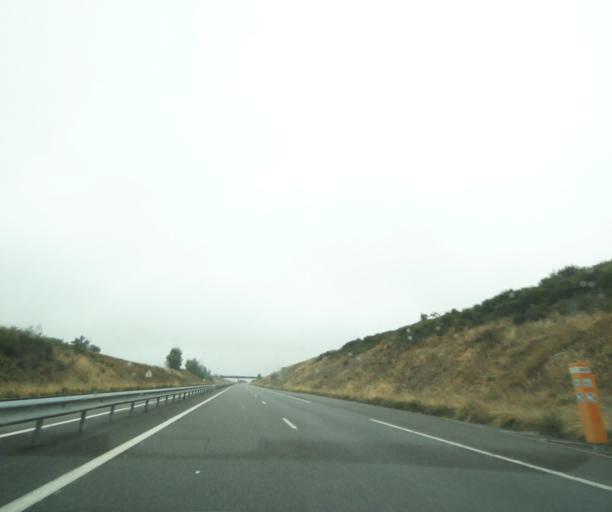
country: FR
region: Midi-Pyrenees
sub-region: Departement du Tarn
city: Carmaux
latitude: 44.0738
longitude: 2.2310
